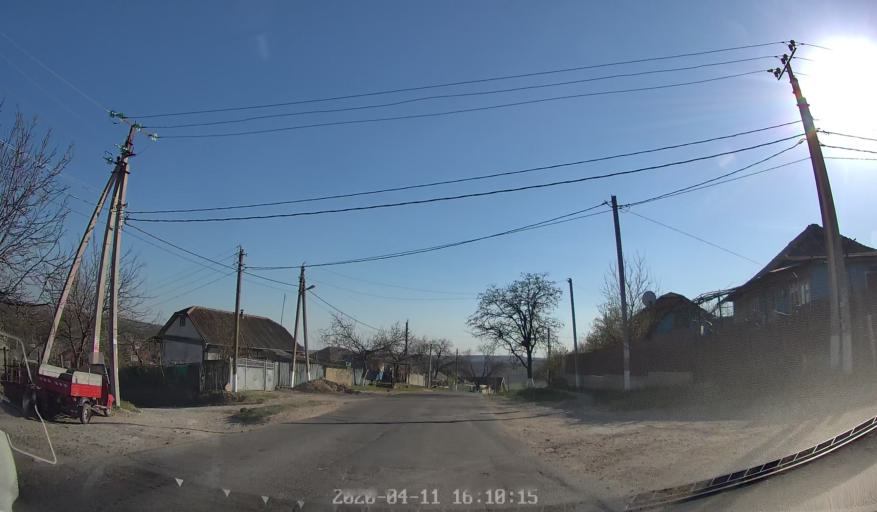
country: MD
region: Chisinau
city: Vadul lui Voda
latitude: 47.0689
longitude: 29.1342
